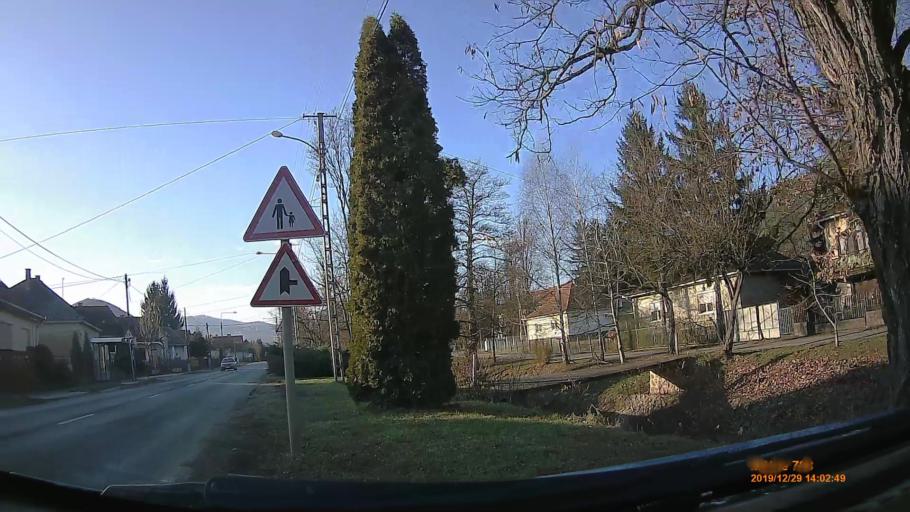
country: HU
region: Heves
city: Parad
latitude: 47.9232
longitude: 20.0369
